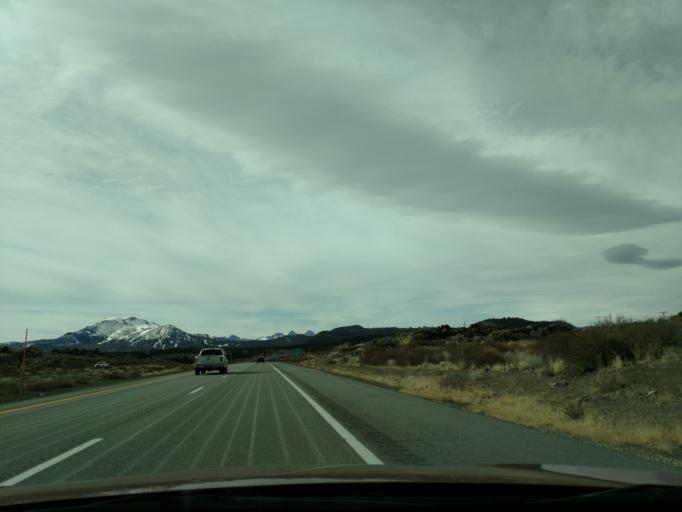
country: US
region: California
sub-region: Mono County
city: Mammoth Lakes
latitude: 37.6370
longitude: -118.8951
